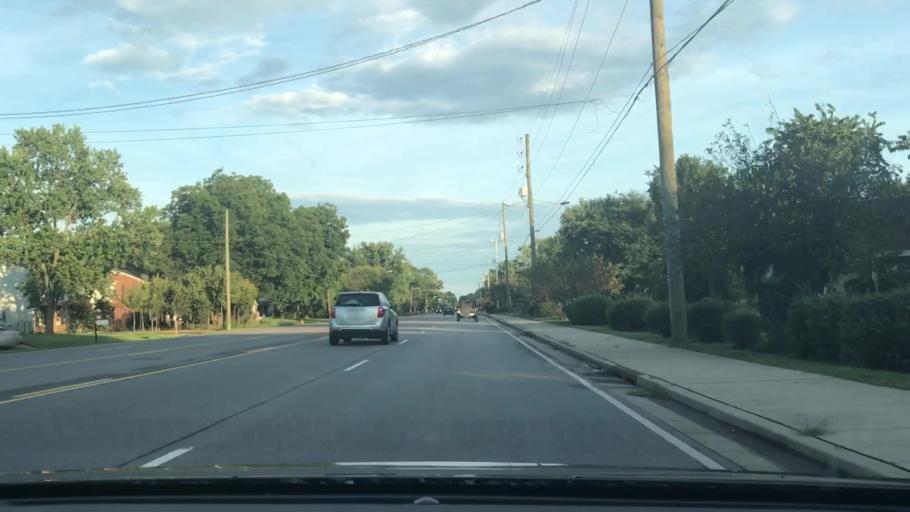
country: US
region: Tennessee
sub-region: Davidson County
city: Oak Hill
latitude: 36.0805
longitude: -86.7505
